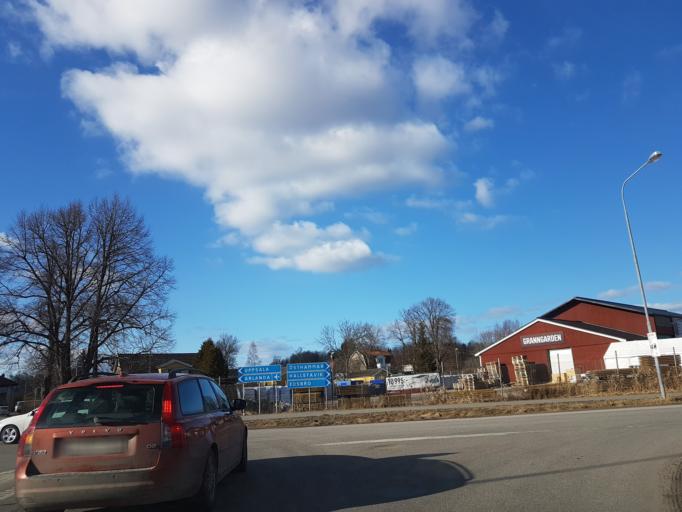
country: SE
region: Stockholm
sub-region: Norrtalje Kommun
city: Rimbo
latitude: 59.7456
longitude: 18.3770
